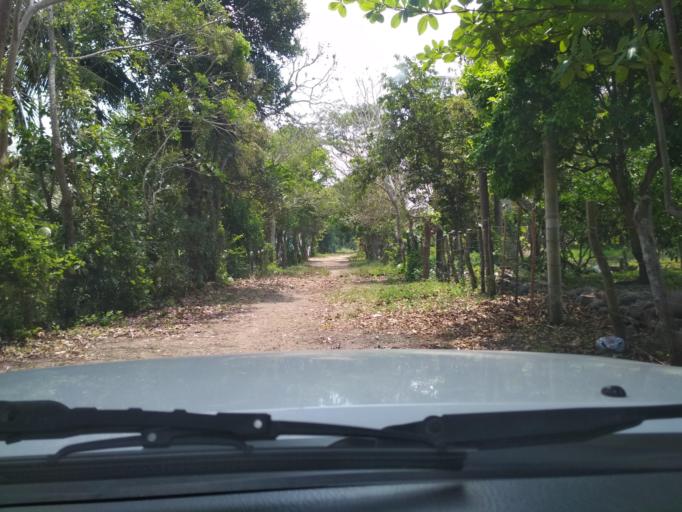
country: MX
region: Veracruz
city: Anton Lizardo
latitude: 19.0055
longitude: -95.9880
